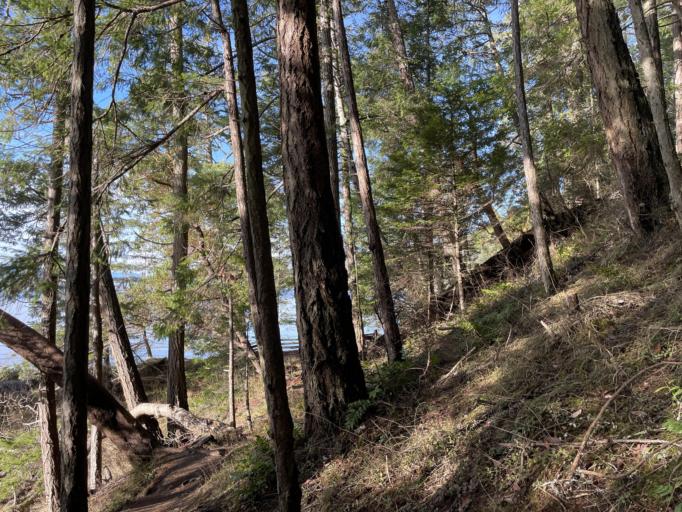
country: CA
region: British Columbia
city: North Saanich
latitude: 48.8989
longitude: -123.4072
